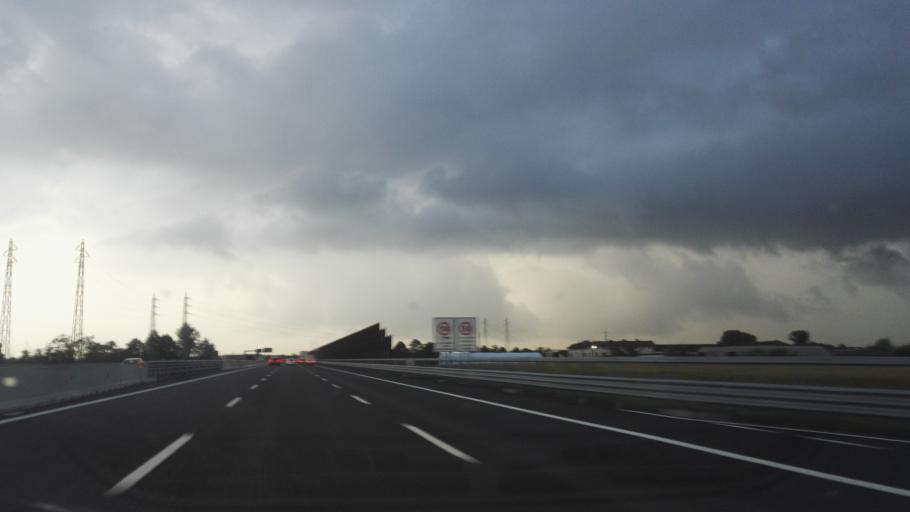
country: IT
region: Lombardy
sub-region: Citta metropolitana di Milano
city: Bellinzago Lombardo
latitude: 45.5240
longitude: 9.4398
